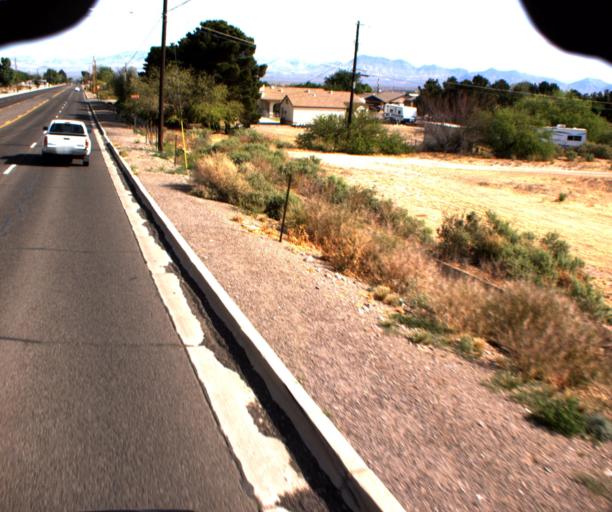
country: US
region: Arizona
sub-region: Graham County
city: Safford
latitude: 32.8062
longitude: -109.7076
